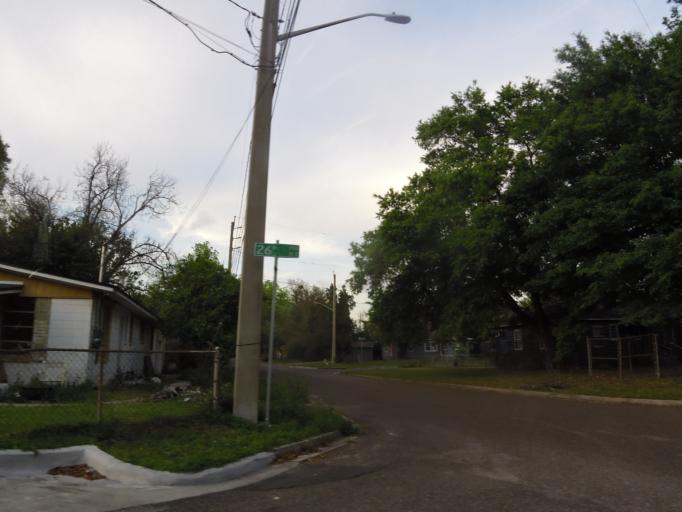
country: US
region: Florida
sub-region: Duval County
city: Jacksonville
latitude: 30.3606
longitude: -81.6307
